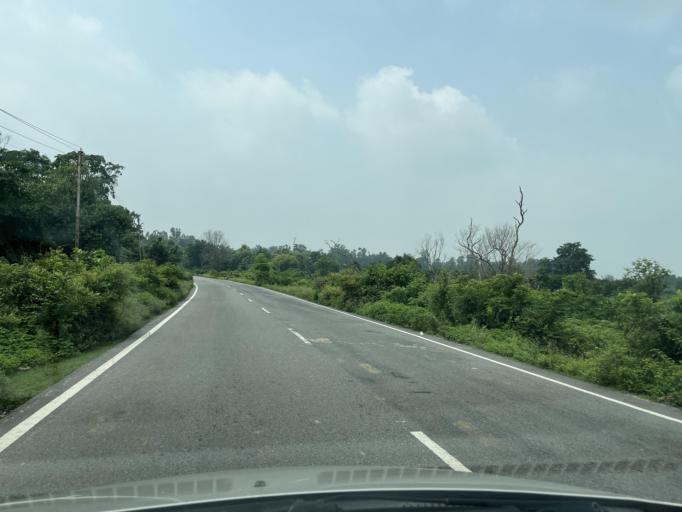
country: IN
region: Uttarakhand
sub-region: Haridwar
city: Sultanpur
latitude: 29.7609
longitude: 78.2708
